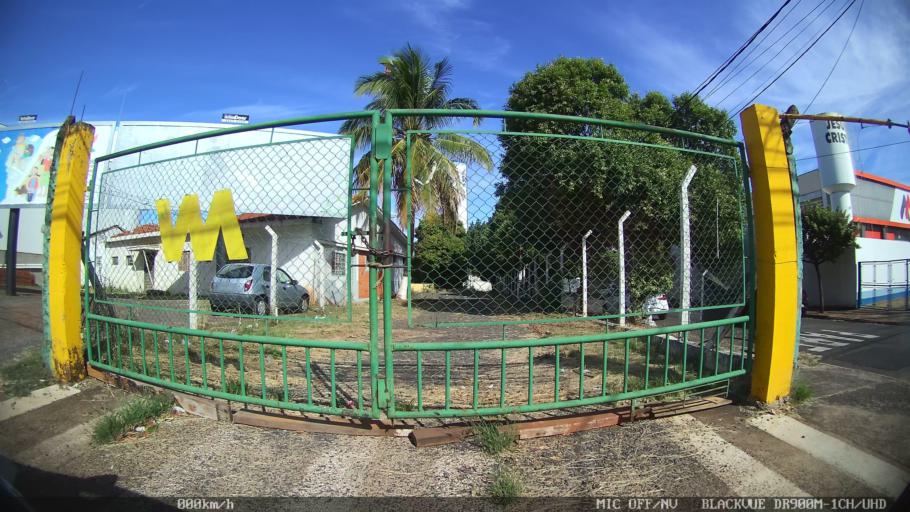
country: BR
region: Sao Paulo
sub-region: Sao Jose Do Rio Preto
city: Sao Jose do Rio Preto
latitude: -20.8020
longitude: -49.3476
